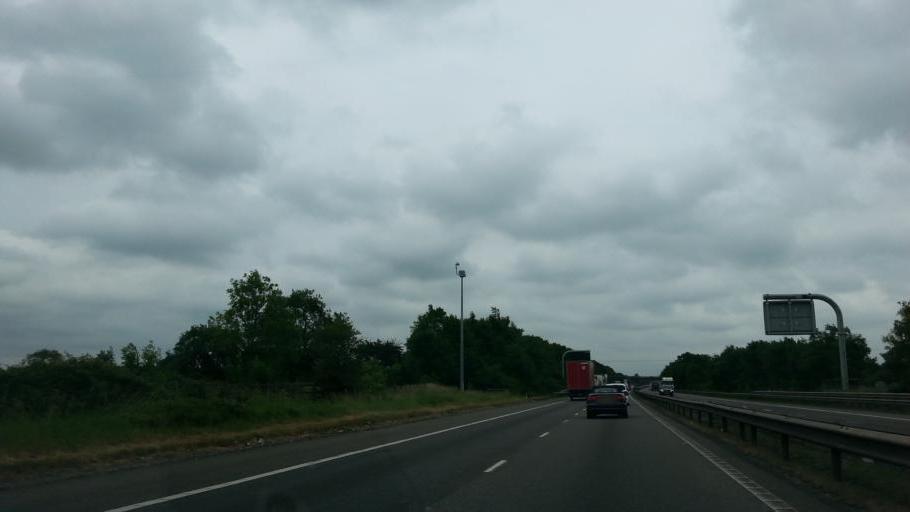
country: GB
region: England
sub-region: Derbyshire
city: Netherseal
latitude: 52.6572
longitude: -1.5827
